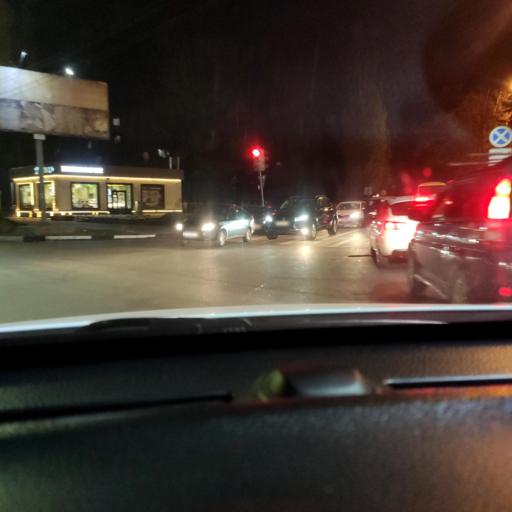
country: RU
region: Voronezj
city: Voronezh
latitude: 51.6794
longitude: 39.2600
